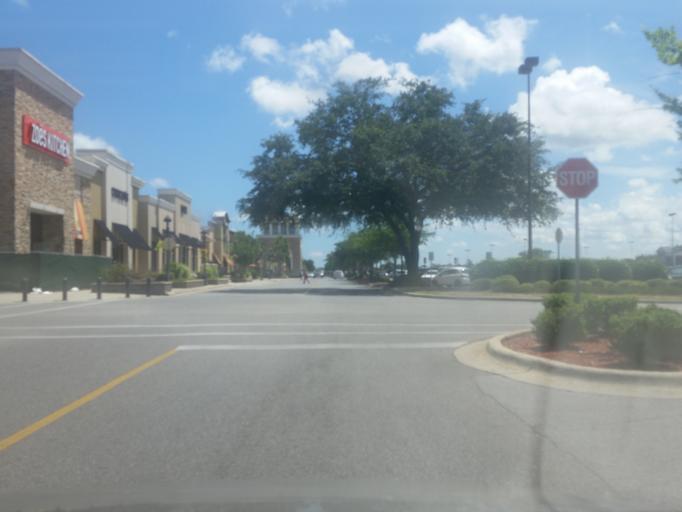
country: US
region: Florida
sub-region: Escambia County
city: Brent
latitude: 30.4769
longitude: -87.2083
